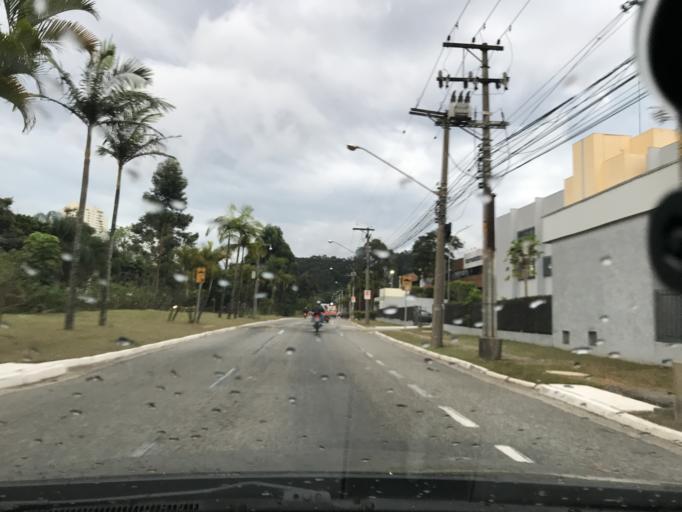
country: BR
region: Sao Paulo
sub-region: Carapicuiba
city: Carapicuiba
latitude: -23.4992
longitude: -46.8309
